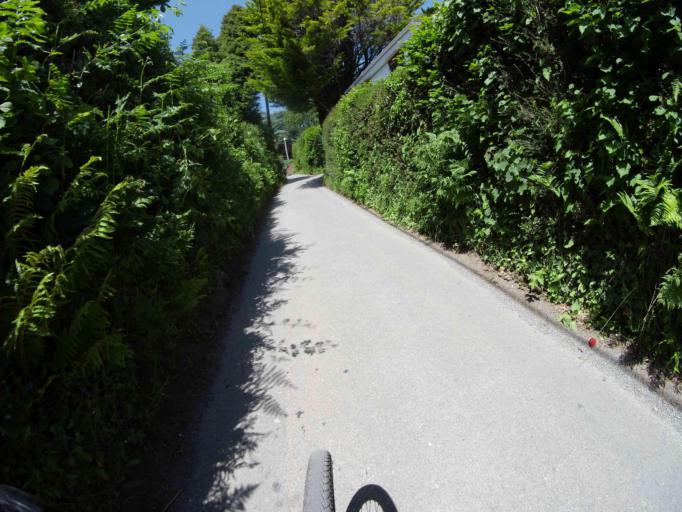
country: GB
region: England
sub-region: Devon
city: Bovey Tracey
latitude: 50.6091
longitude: -3.7093
